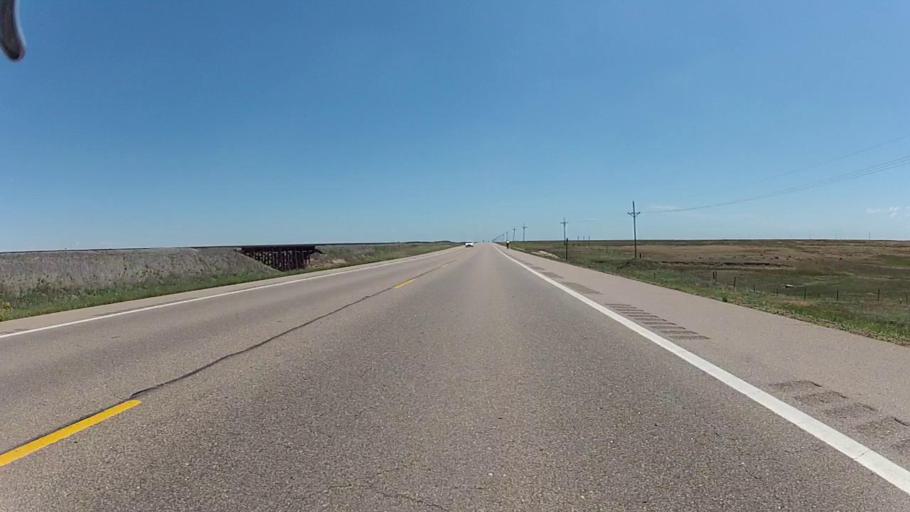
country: US
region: Kansas
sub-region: Ford County
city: Dodge City
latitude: 37.7101
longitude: -100.1191
